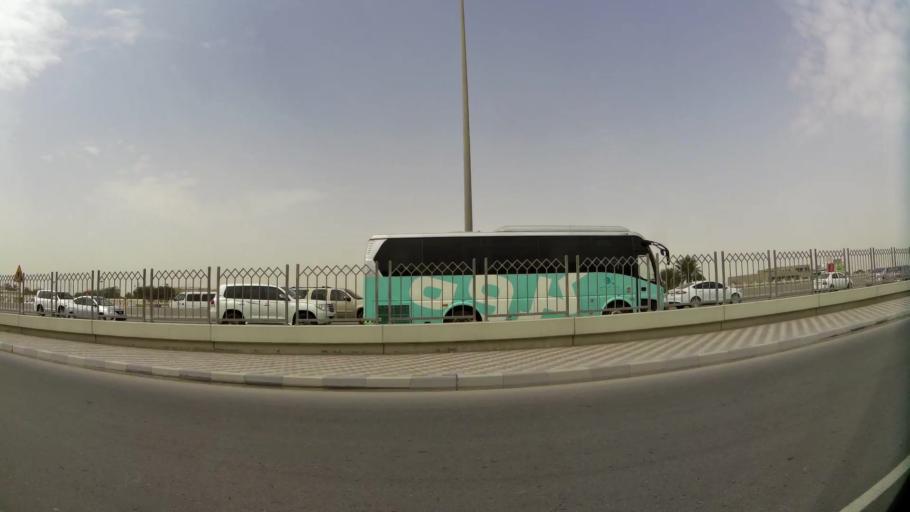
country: QA
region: Baladiyat ar Rayyan
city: Ar Rayyan
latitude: 25.3062
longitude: 51.4732
